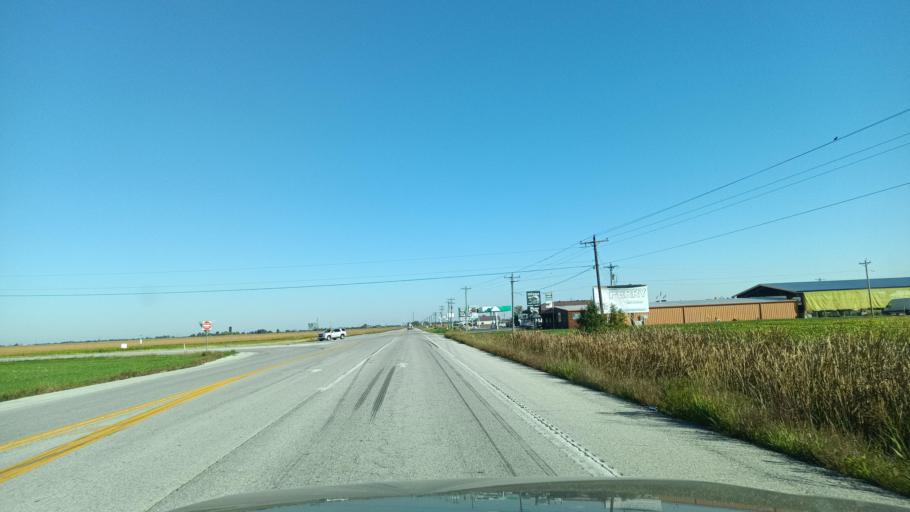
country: US
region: Missouri
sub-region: Audrain County
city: Vandalia
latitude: 39.4284
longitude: -91.6364
